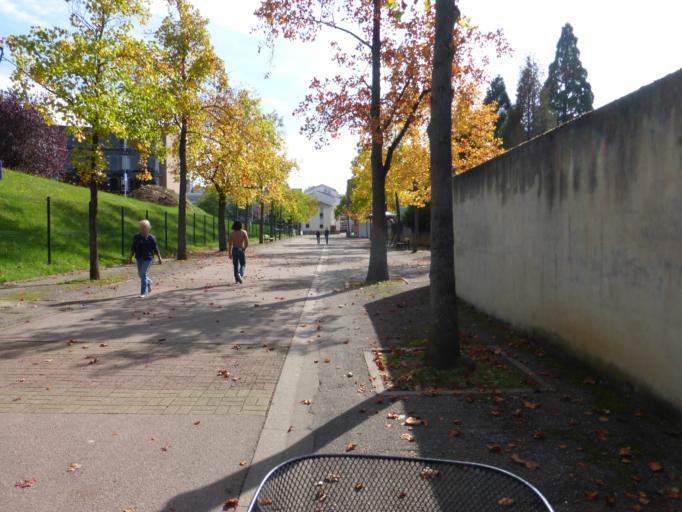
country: FR
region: Lorraine
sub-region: Departement de Meurthe-et-Moselle
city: Nancy
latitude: 48.6788
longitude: 6.1725
